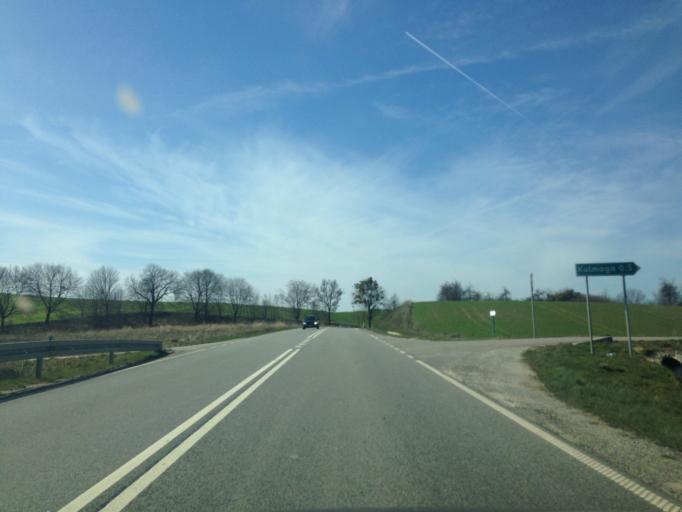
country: PL
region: Pomeranian Voivodeship
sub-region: Powiat starogardzki
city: Smetowo Graniczne
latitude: 53.7353
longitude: 18.7162
